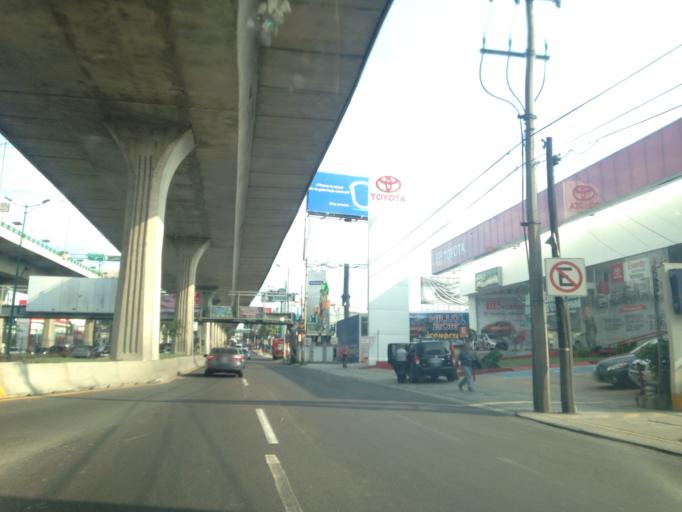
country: MX
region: Mexico
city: Naucalpan de Juarez
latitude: 19.4837
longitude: -99.2343
